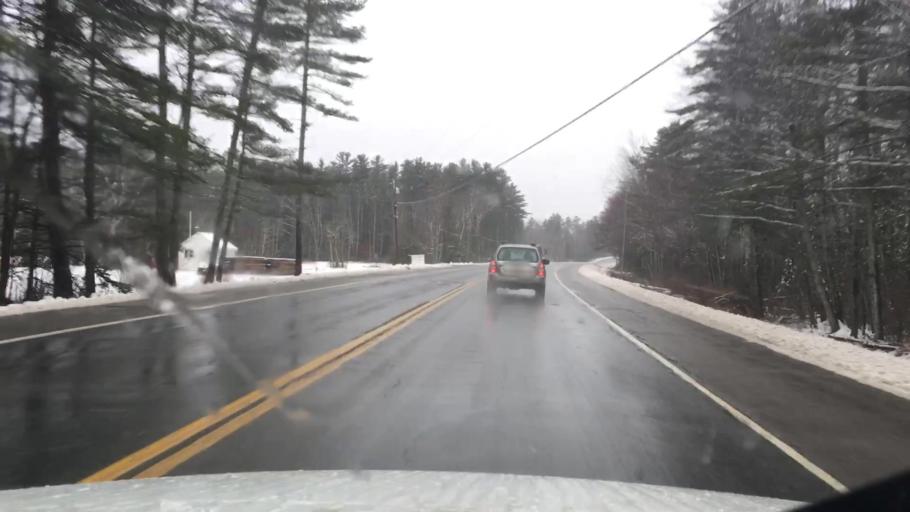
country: US
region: Maine
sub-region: Knox County
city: Warren
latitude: 44.1601
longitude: -69.1798
